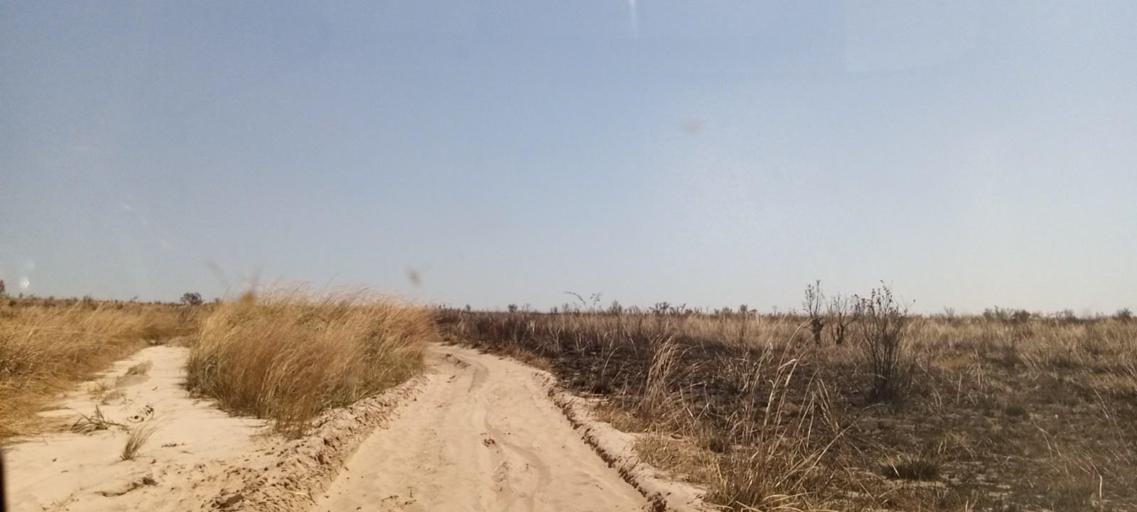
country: CD
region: Kasai-Oriental
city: Kabinda
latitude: -5.9398
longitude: 24.8109
